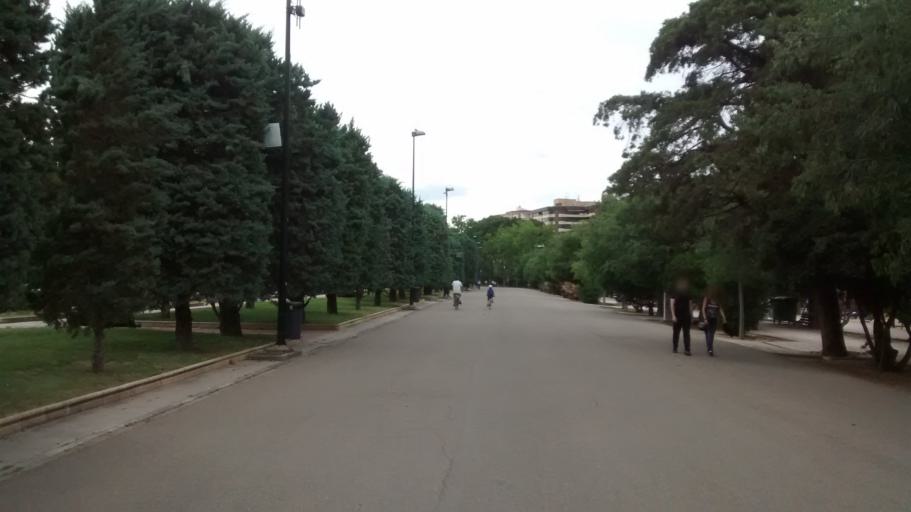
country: ES
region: Aragon
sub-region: Provincia de Zaragoza
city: Delicias
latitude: 41.6352
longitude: -0.8949
